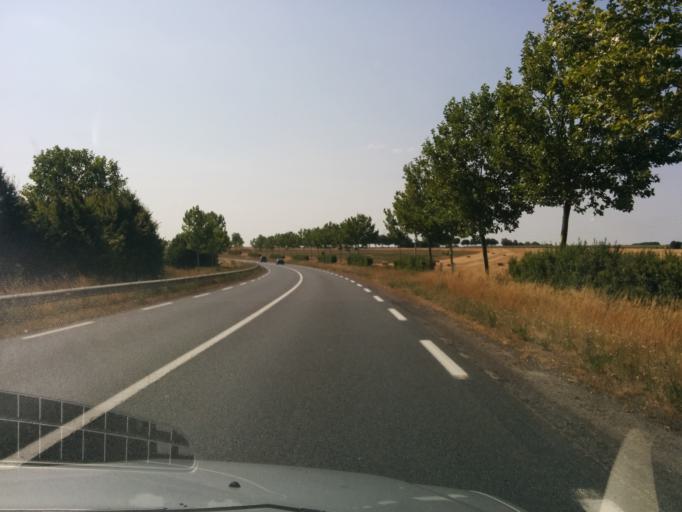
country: FR
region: Poitou-Charentes
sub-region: Departement de la Vienne
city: Neuville-de-Poitou
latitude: 46.7123
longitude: 0.2239
